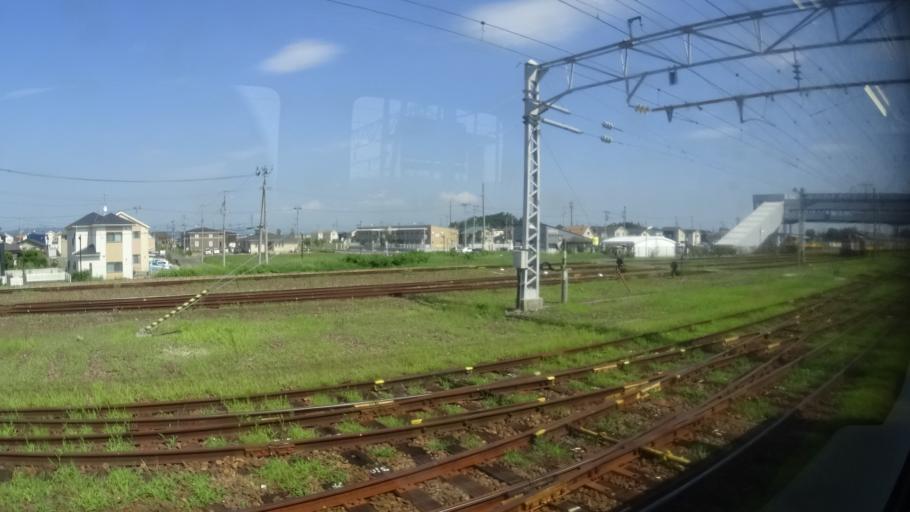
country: JP
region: Miyagi
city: Kogota
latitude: 38.5423
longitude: 141.0644
